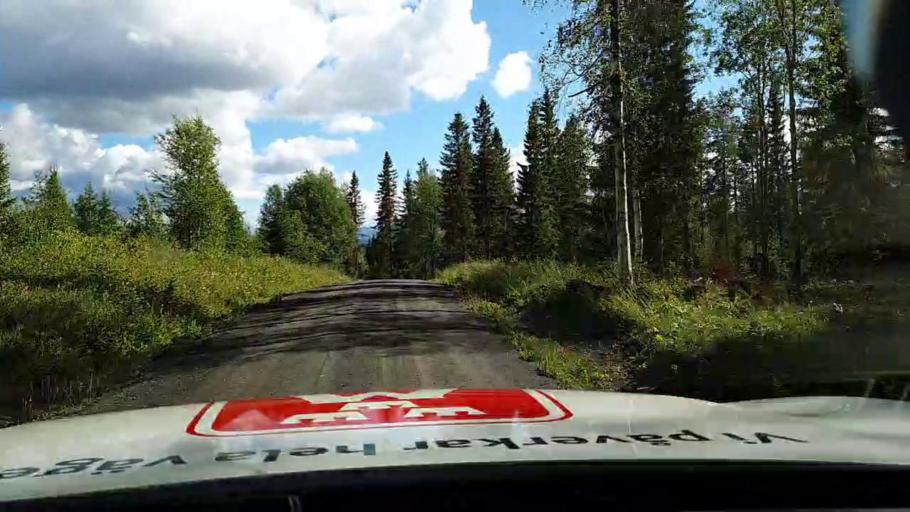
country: SE
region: Jaemtland
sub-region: Krokoms Kommun
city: Valla
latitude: 63.3289
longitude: 13.7347
